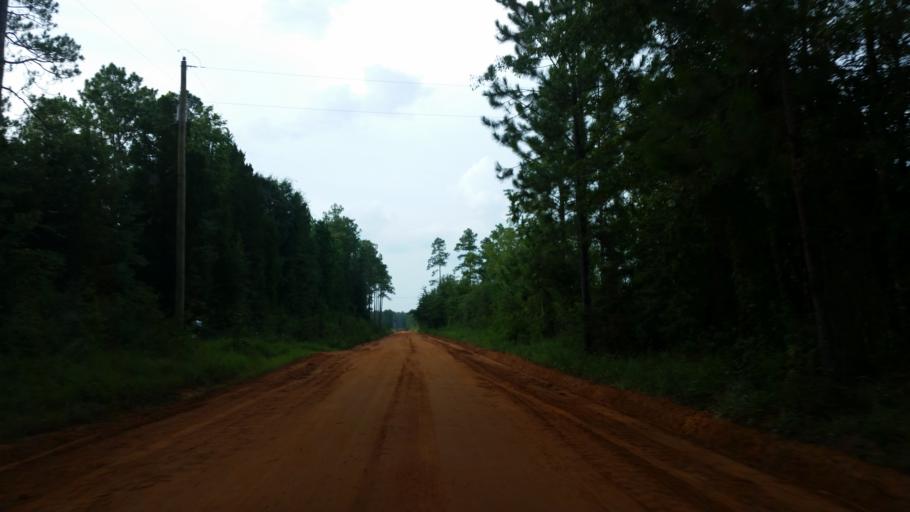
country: US
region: Alabama
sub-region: Baldwin County
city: Bay Minette
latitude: 30.8245
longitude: -87.5689
